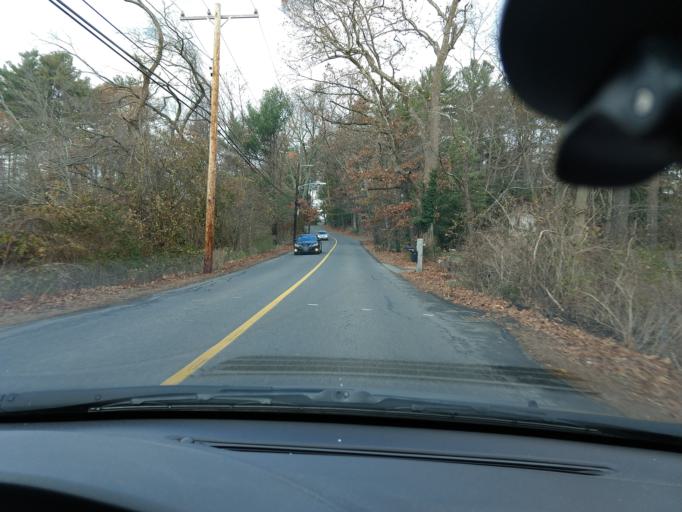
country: US
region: Massachusetts
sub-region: Middlesex County
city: West Concord
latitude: 42.4743
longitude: -71.3786
